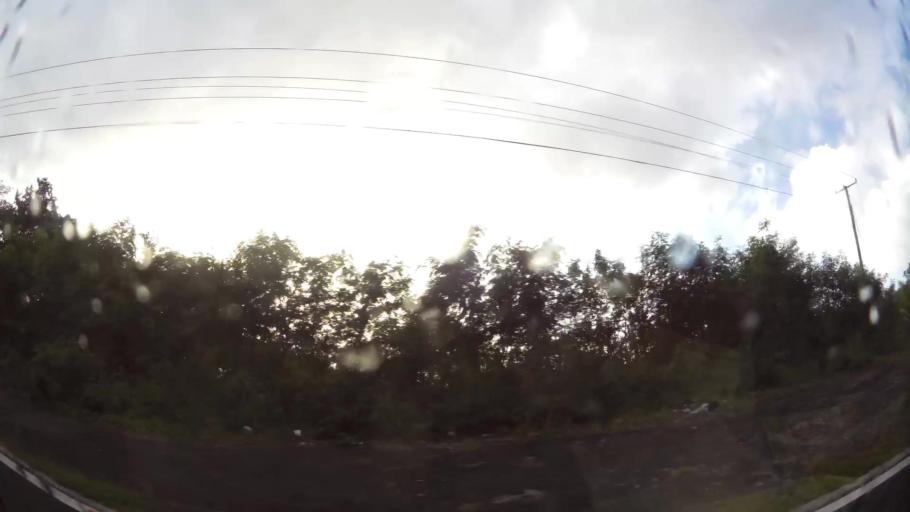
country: DM
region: Saint Paul
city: Mahaut
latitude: 15.3780
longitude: -61.4072
